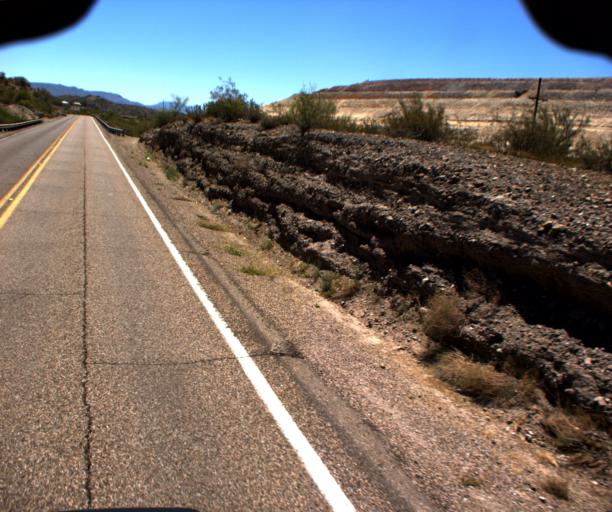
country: US
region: Arizona
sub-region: Pinal County
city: Kearny
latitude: 33.0050
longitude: -110.7973
